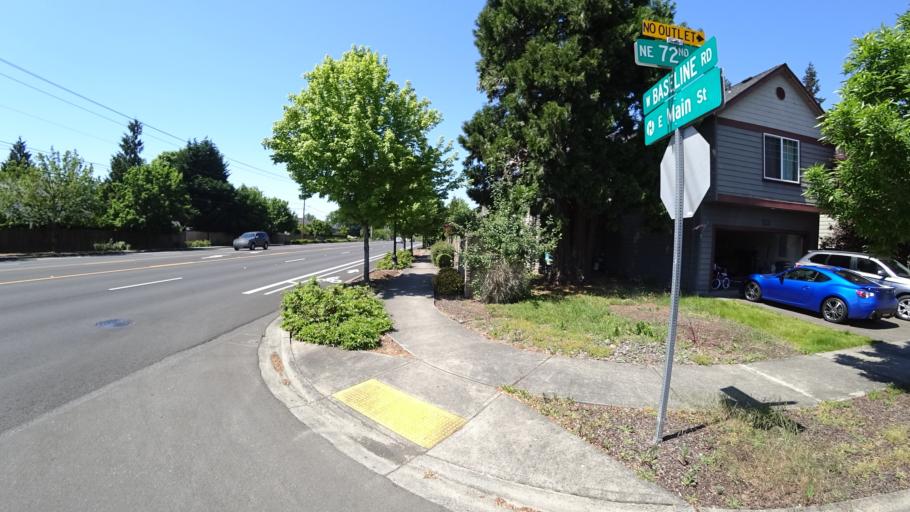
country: US
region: Oregon
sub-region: Washington County
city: Rockcreek
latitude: 45.5178
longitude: -122.9063
